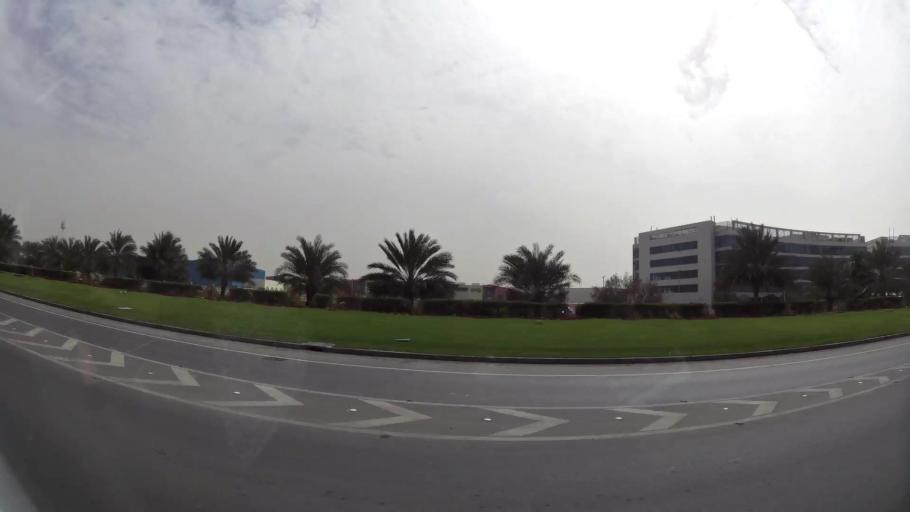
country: AE
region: Abu Dhabi
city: Abu Dhabi
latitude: 24.3240
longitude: 54.5226
